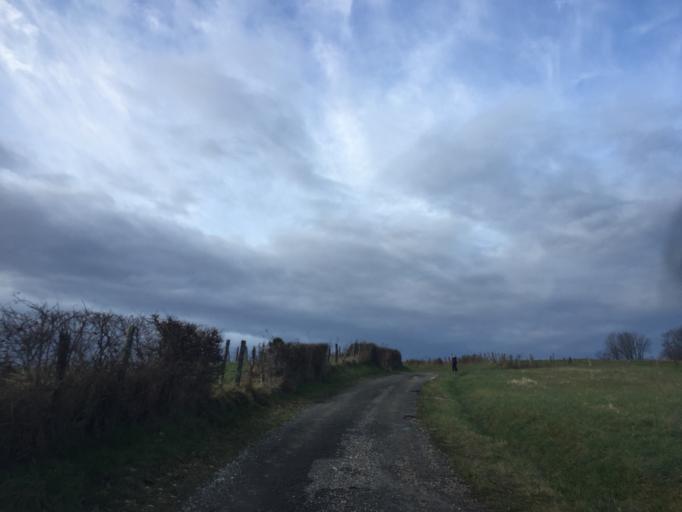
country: FR
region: Franche-Comte
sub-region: Departement du Jura
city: Arbois
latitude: 46.9369
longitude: 5.6878
